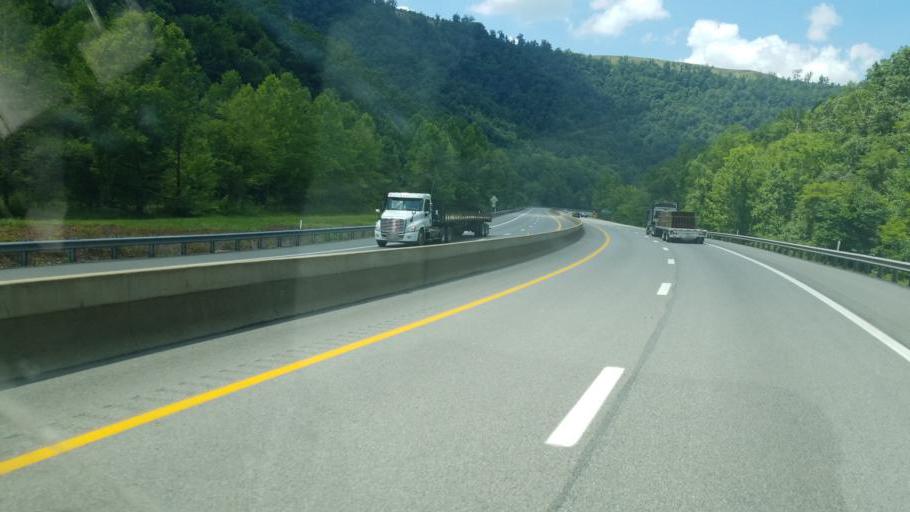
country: US
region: West Virginia
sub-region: Kanawha County
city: Montgomery
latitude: 38.0890
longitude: -81.3873
